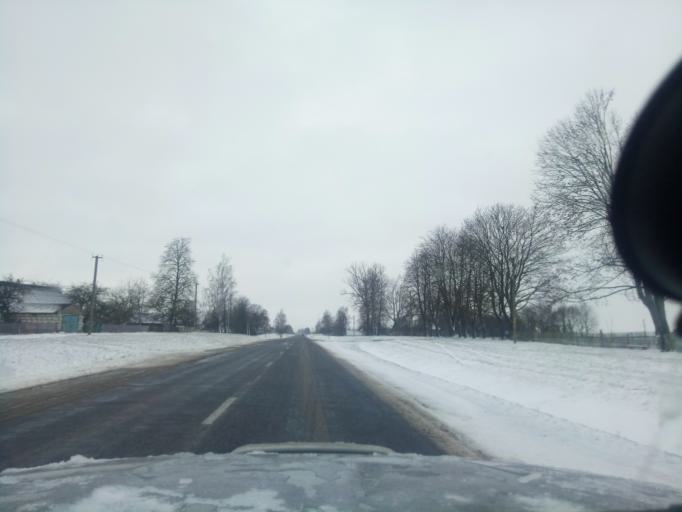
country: BY
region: Minsk
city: Klyetsk
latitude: 53.1196
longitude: 26.6649
